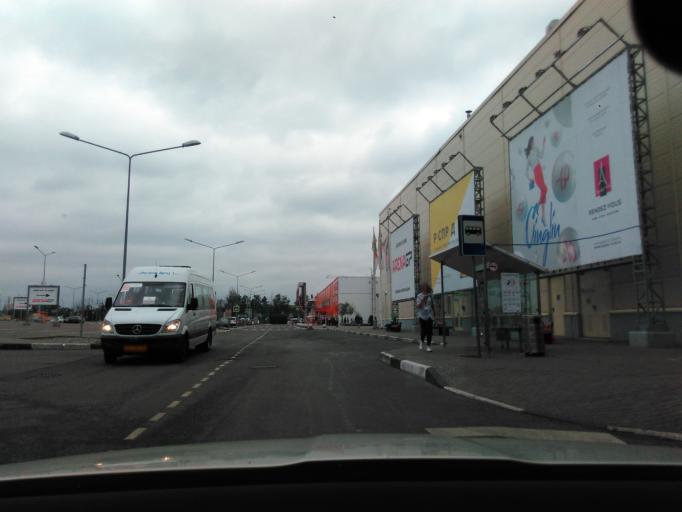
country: RU
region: Moscow
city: Khimki
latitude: 55.9108
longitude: 37.3941
